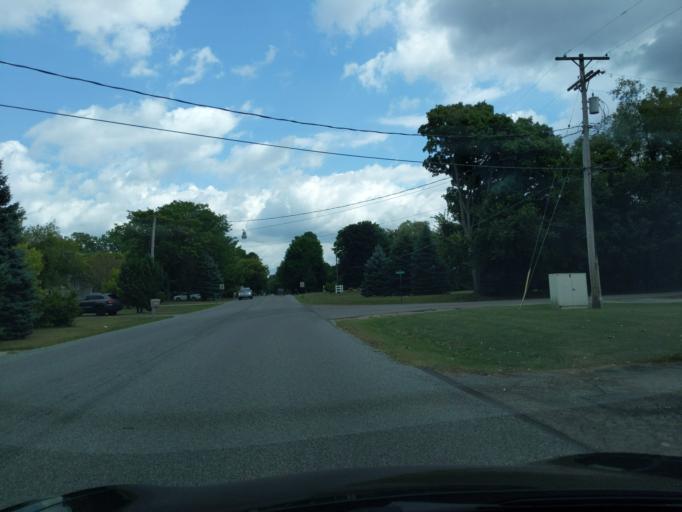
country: US
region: Michigan
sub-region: Eaton County
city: Dimondale
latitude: 42.6620
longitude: -84.5880
